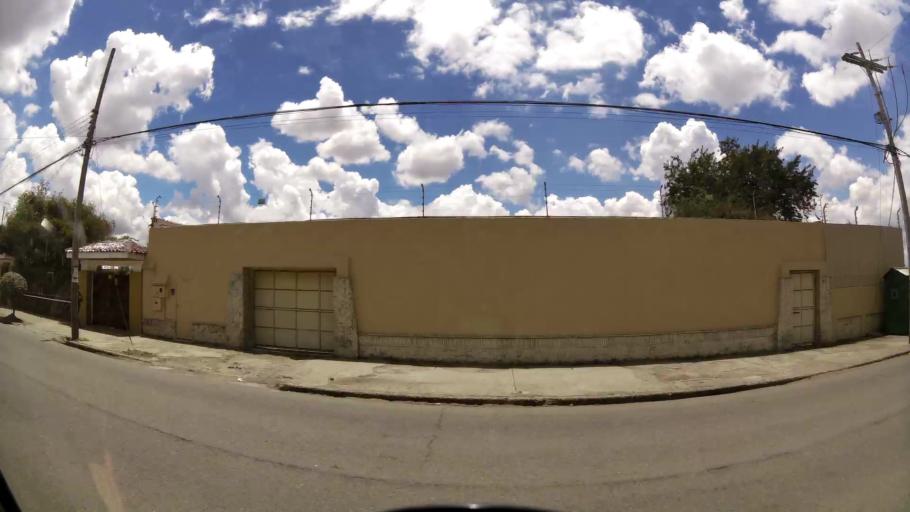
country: EC
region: Azuay
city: Cuenca
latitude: -2.8847
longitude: -79.0044
